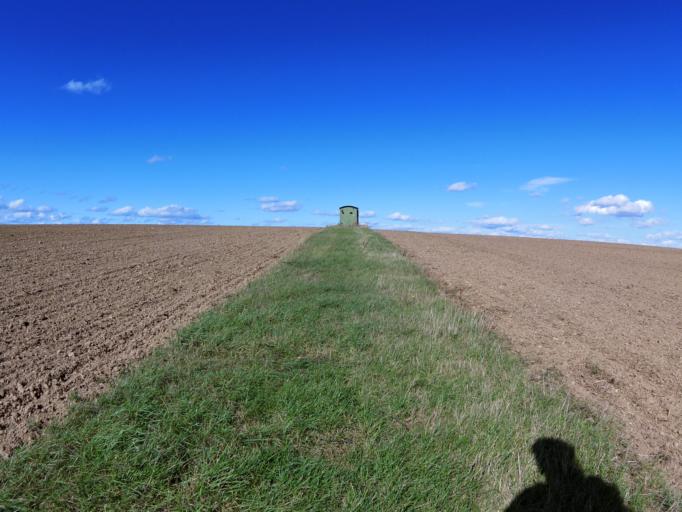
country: DE
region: Bavaria
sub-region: Regierungsbezirk Unterfranken
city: Erlabrunn
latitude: 49.8322
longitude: 9.8266
